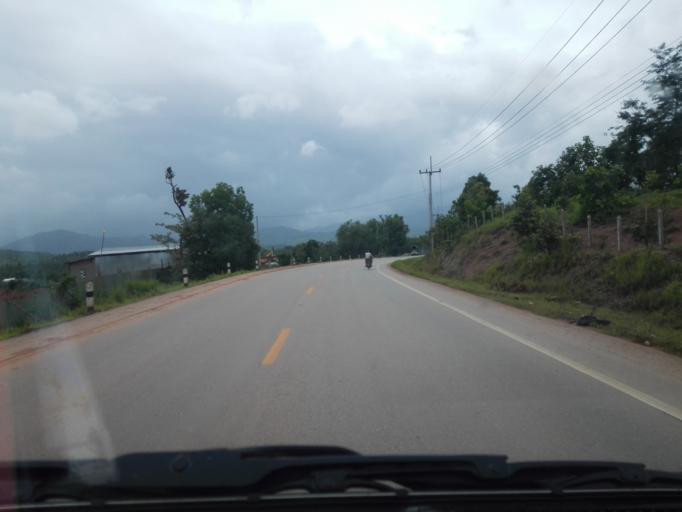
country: TH
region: Tak
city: Mae Sot
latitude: 16.6906
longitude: 98.4465
